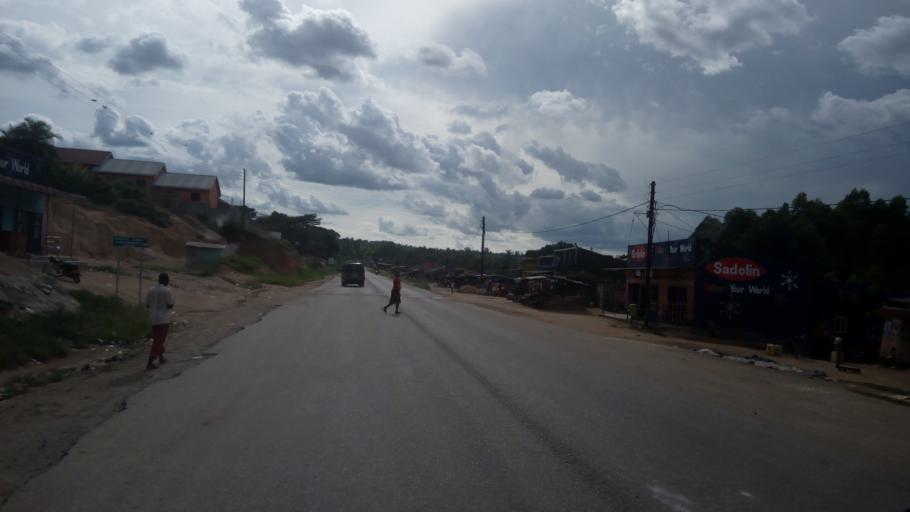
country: UG
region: Central Region
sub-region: Mubende District
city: Mubende
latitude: 0.4973
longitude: 31.2858
